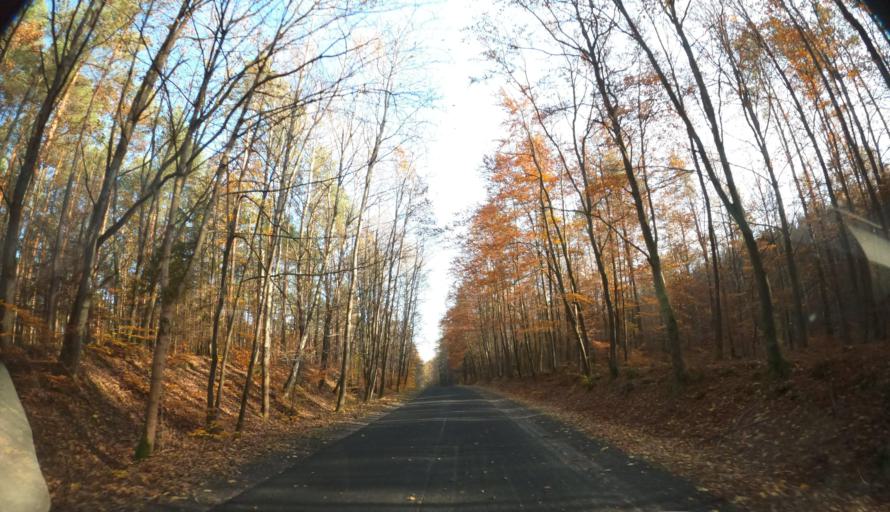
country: PL
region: West Pomeranian Voivodeship
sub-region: Powiat koszalinski
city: Polanow
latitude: 54.2411
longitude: 16.7150
